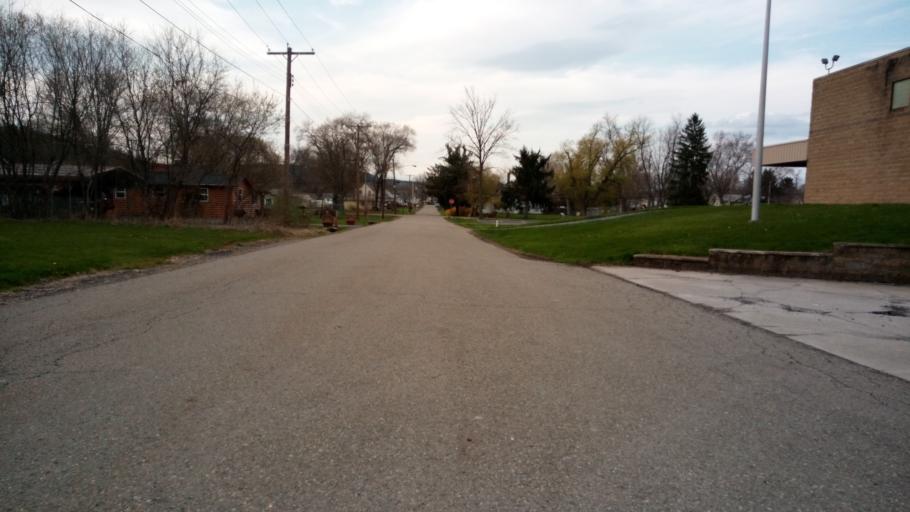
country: US
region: New York
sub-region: Chemung County
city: Southport
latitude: 42.0664
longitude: -76.8177
